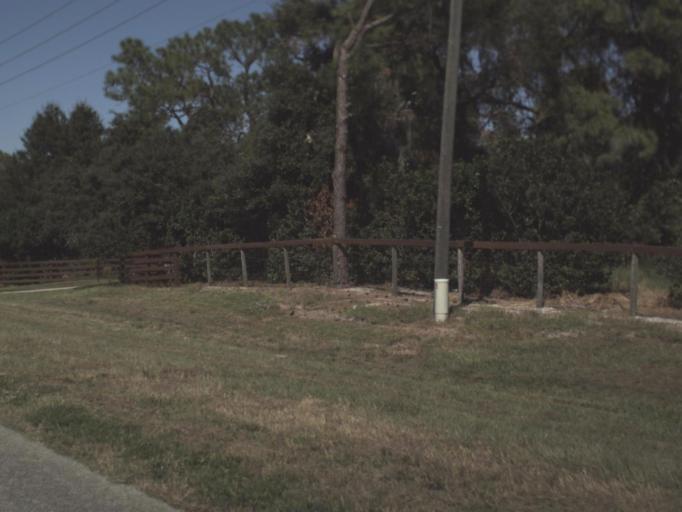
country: US
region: Florida
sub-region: Highlands County
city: Lake Placid
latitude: 27.2472
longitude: -81.3375
